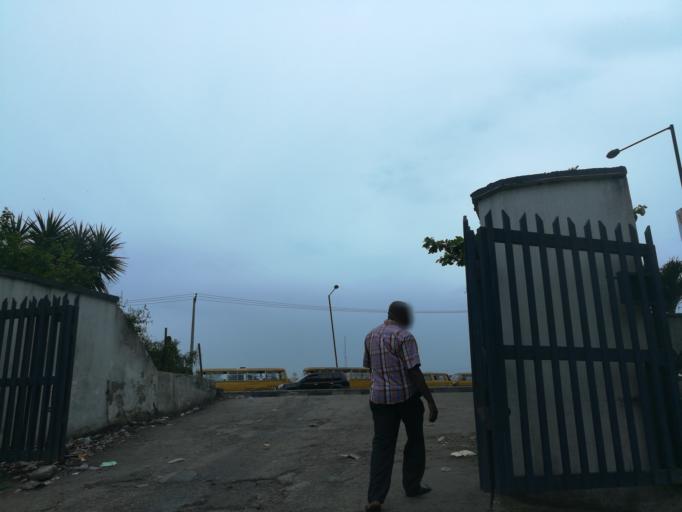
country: NG
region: Lagos
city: Ebute Metta
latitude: 6.4789
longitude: 3.3832
